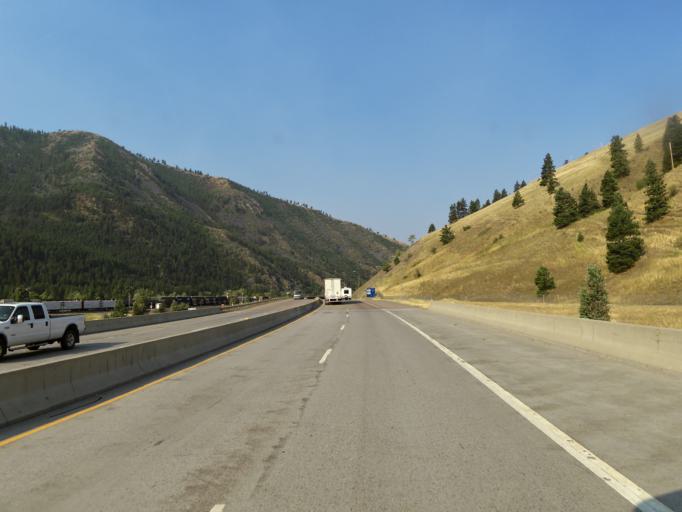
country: US
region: Montana
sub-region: Missoula County
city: East Missoula
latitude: 46.8669
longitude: -113.9512
